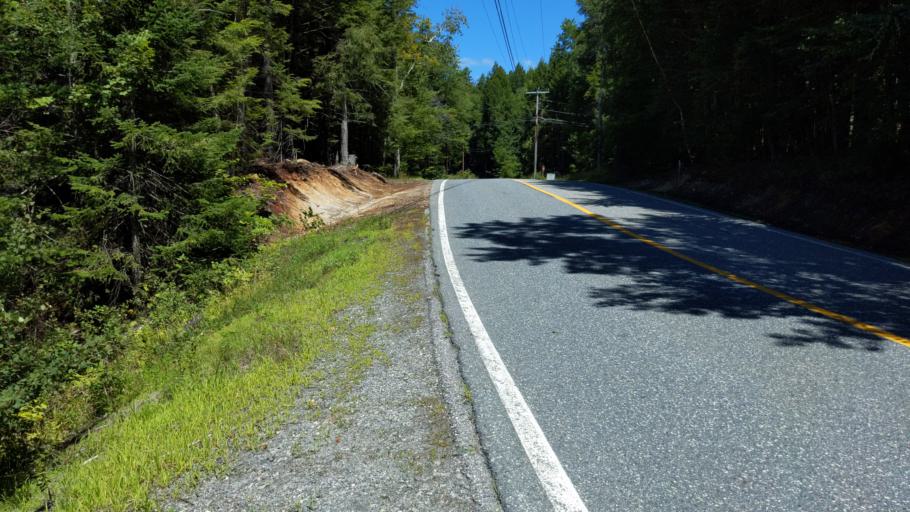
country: US
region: New Hampshire
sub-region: Sullivan County
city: Grantham
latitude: 43.5130
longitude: -72.1060
